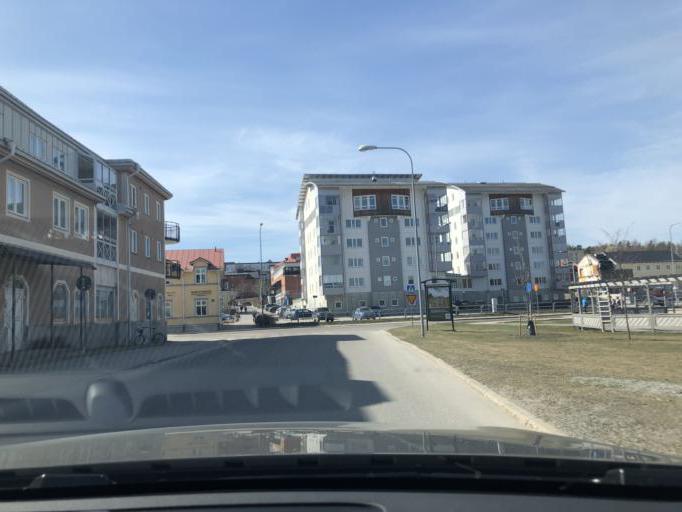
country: SE
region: Gaevleborg
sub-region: Hudiksvalls Kommun
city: Hudiksvall
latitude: 61.7293
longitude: 17.1064
